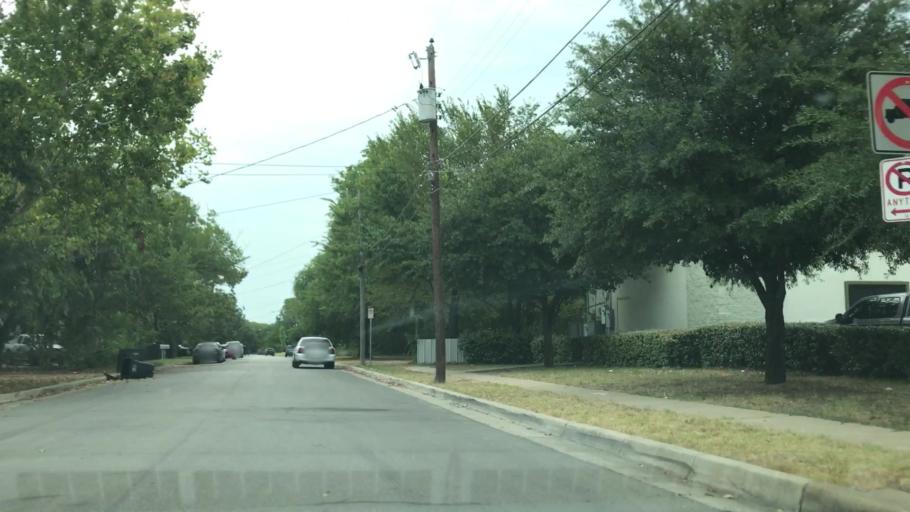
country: US
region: Texas
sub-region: Tarrant County
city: Haltom City
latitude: 32.7661
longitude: -97.2876
